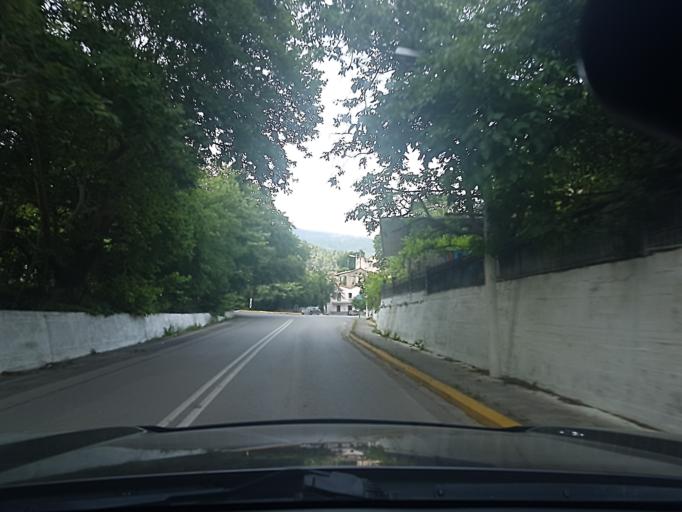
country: GR
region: Central Greece
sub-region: Nomos Evvoias
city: Yimnon
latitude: 38.5796
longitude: 23.8353
